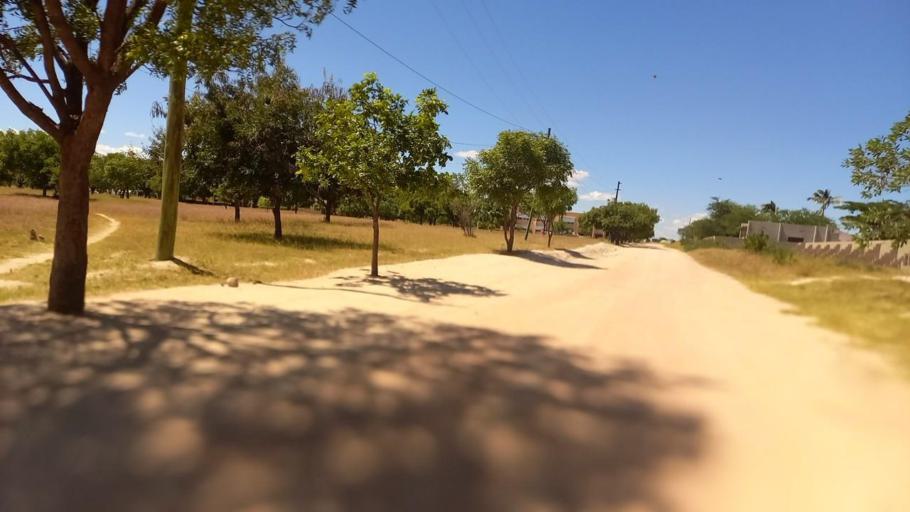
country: TZ
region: Dodoma
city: Dodoma
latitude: -6.1173
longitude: 35.7423
